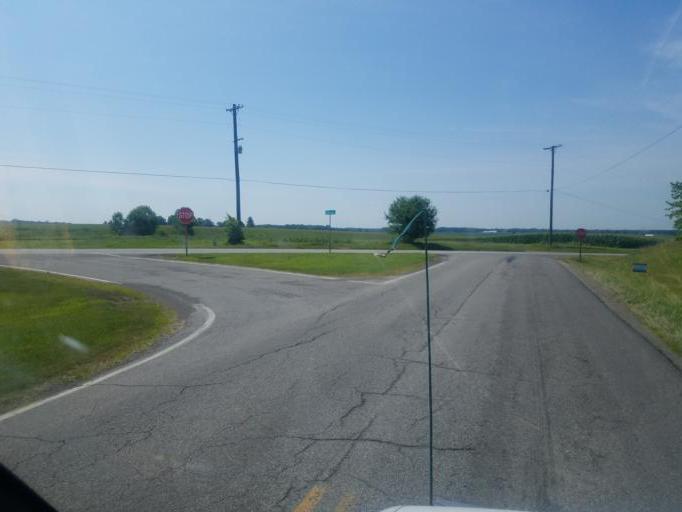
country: US
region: Ohio
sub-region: Union County
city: Marysville
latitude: 40.2834
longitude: -83.3503
